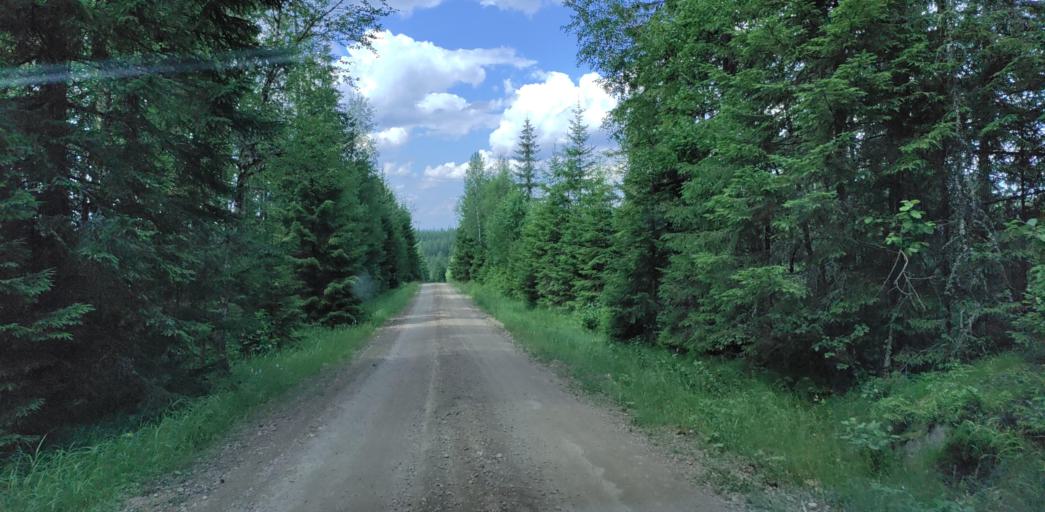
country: SE
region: Vaermland
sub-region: Hagfors Kommun
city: Ekshaerad
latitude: 60.0896
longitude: 13.3442
